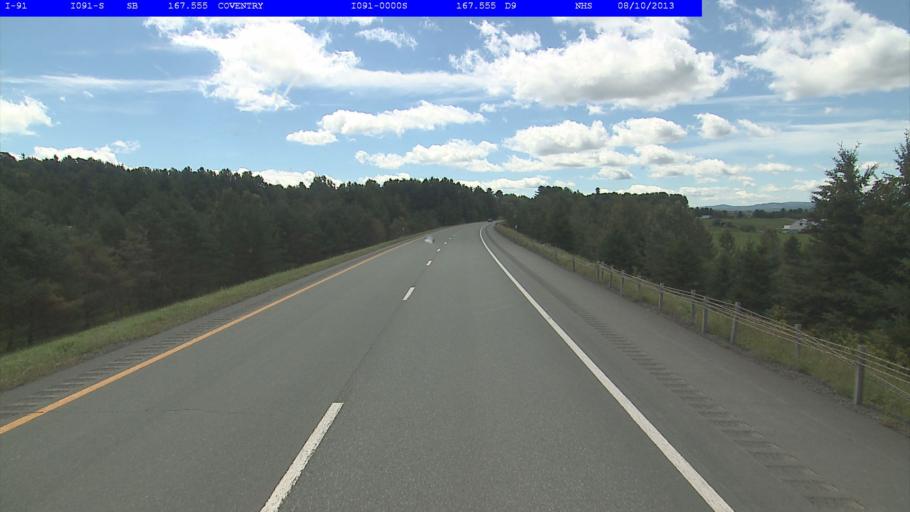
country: US
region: Vermont
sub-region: Orleans County
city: Newport
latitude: 44.8877
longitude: -72.1725
